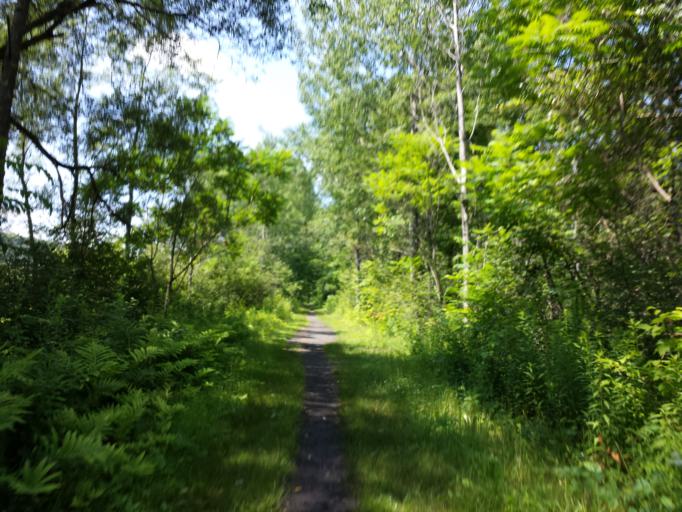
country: US
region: Vermont
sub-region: Rutland County
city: Castleton
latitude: 43.5957
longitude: -73.1906
